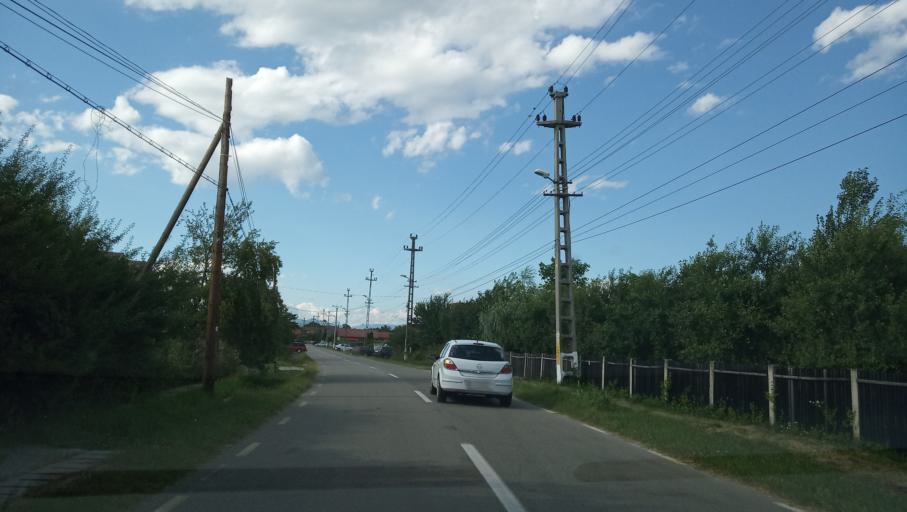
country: RO
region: Gorj
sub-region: Comuna Turcinesti
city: Turcinesti
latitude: 45.0586
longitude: 23.3483
